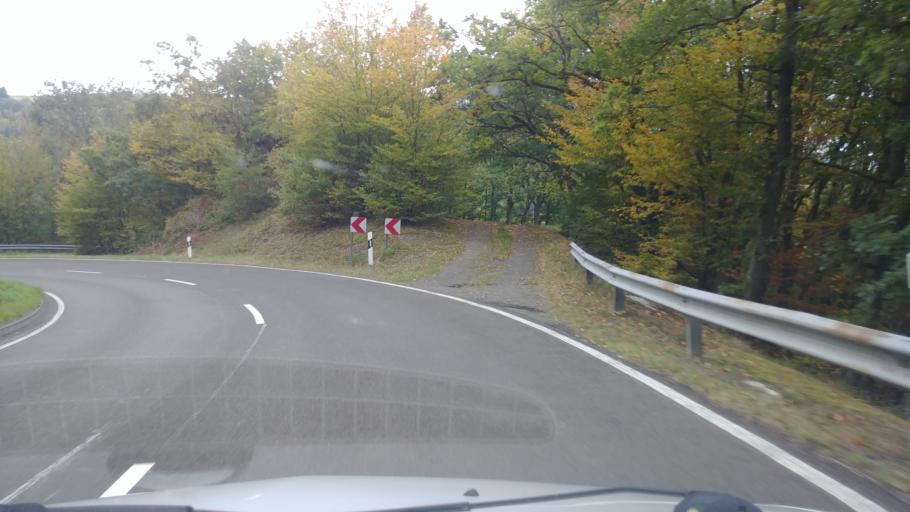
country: DE
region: Rheinland-Pfalz
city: Horath
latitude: 49.8044
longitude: 6.9840
